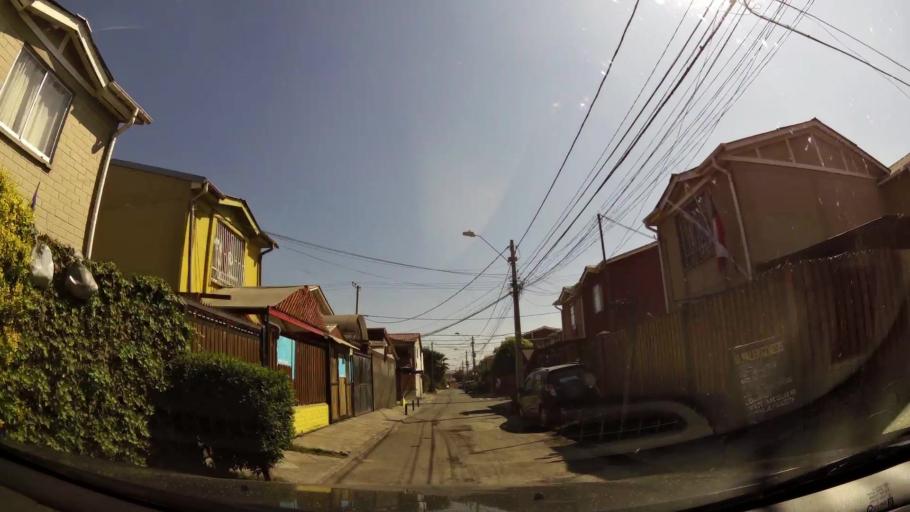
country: CL
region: Santiago Metropolitan
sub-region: Provincia de Santiago
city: Lo Prado
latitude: -33.3515
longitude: -70.7361
